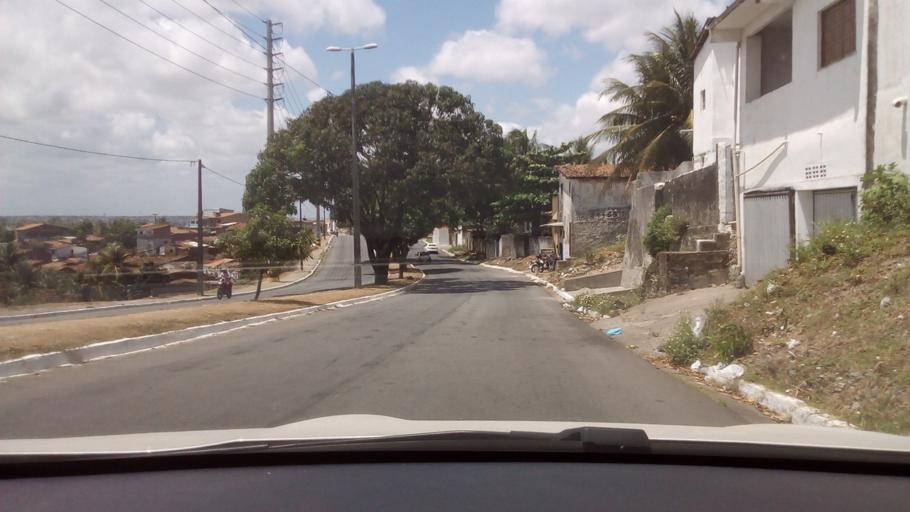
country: BR
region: Paraiba
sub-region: Joao Pessoa
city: Joao Pessoa
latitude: -7.1254
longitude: -34.8876
